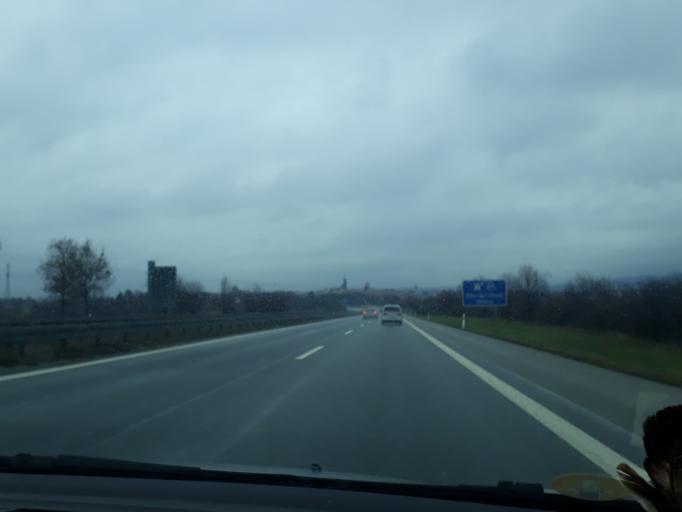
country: DE
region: Saxony
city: Bautzen
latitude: 51.1874
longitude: 14.3885
